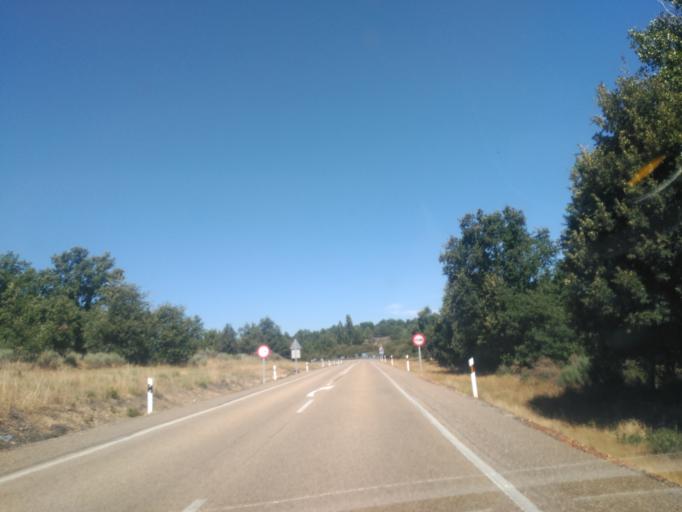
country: ES
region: Castille and Leon
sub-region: Provincia de Zamora
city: Ferreras de Arriba
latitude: 41.9522
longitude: -6.2032
